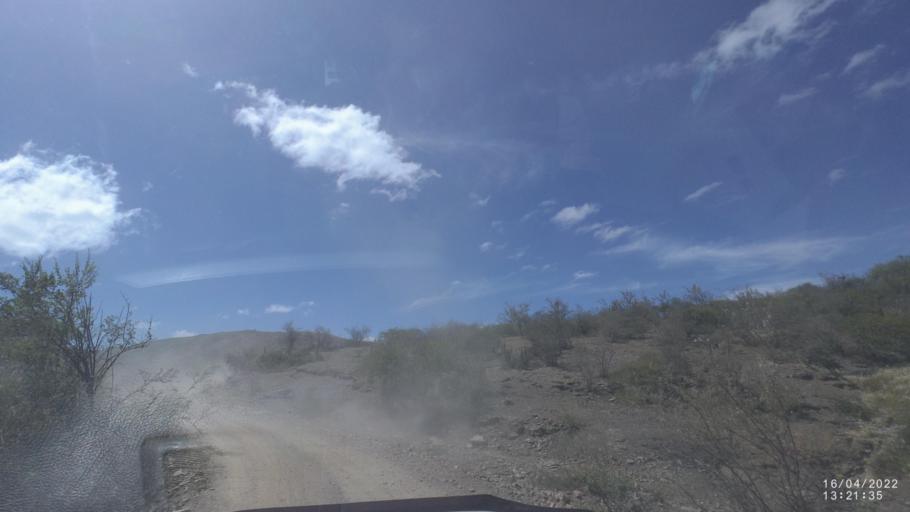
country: BO
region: Cochabamba
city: Mizque
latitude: -17.9921
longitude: -65.6101
